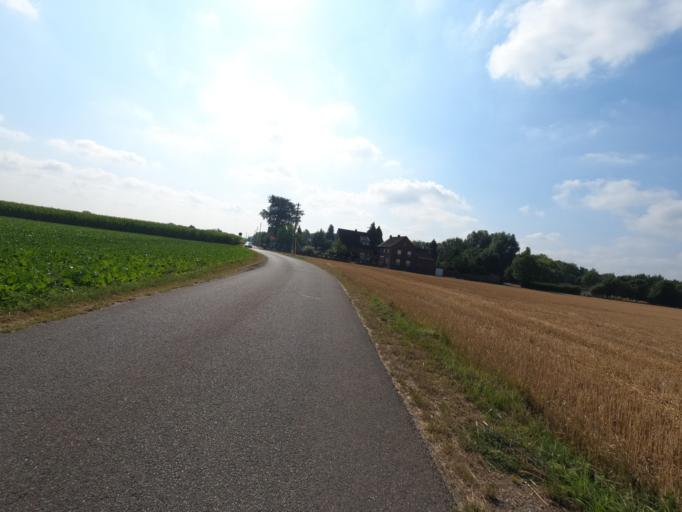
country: DE
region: North Rhine-Westphalia
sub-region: Regierungsbezirk Koln
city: Heinsberg
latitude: 51.0857
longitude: 6.0847
